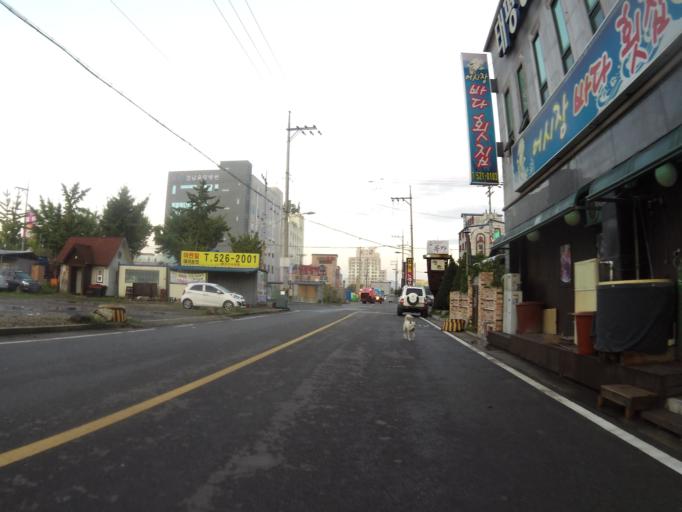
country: KR
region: Gyeongsangnam-do
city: Naeso
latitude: 35.3917
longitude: 128.4759
